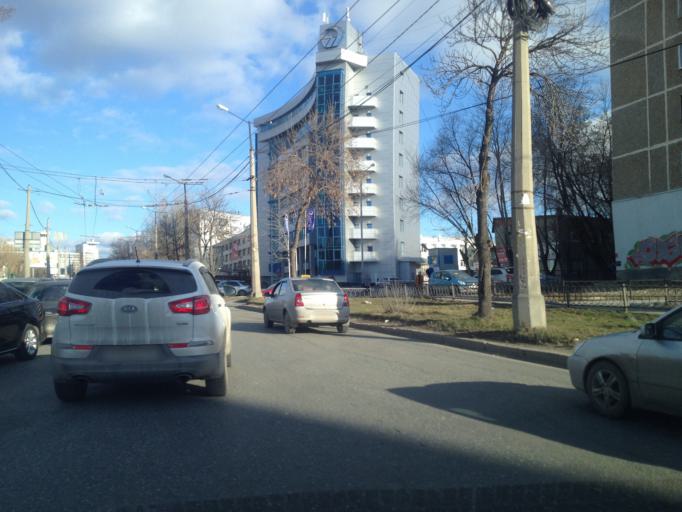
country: RU
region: Sverdlovsk
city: Yekaterinburg
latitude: 56.8229
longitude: 60.5707
